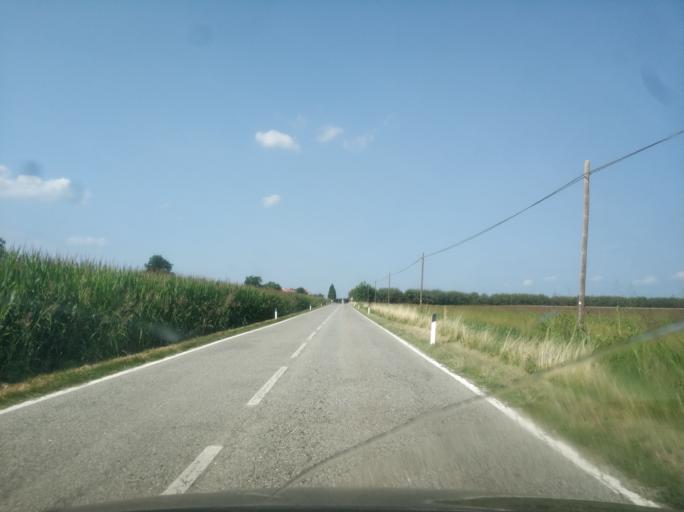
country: IT
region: Piedmont
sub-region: Provincia di Cuneo
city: Caraglio
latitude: 44.4461
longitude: 7.4547
